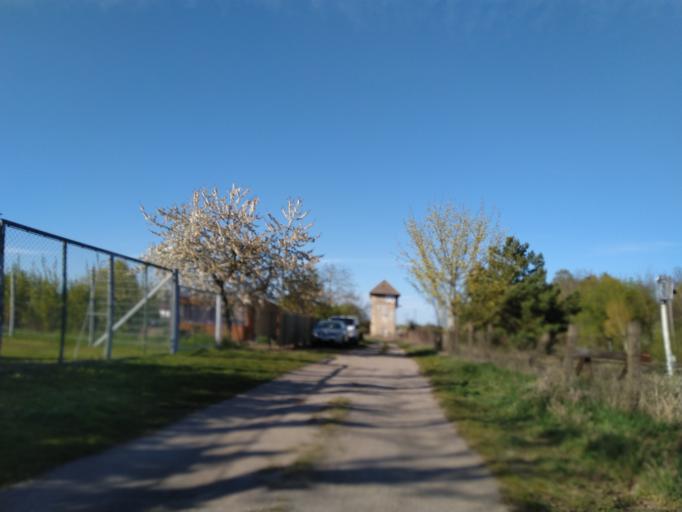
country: DE
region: Brandenburg
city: Wriezen
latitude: 52.7096
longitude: 14.1366
